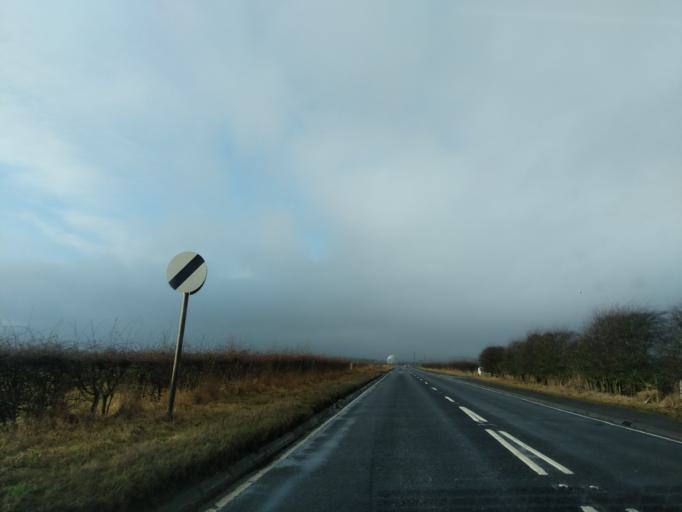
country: GB
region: Scotland
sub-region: Perth and Kinross
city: Kinross
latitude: 56.2090
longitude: -3.4452
